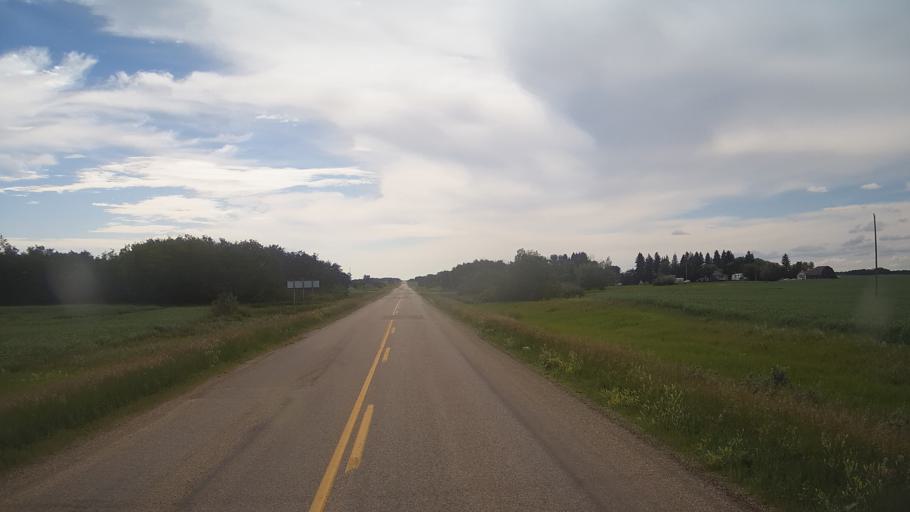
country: CA
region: Saskatchewan
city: Melville
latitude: 51.2102
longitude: -102.8186
